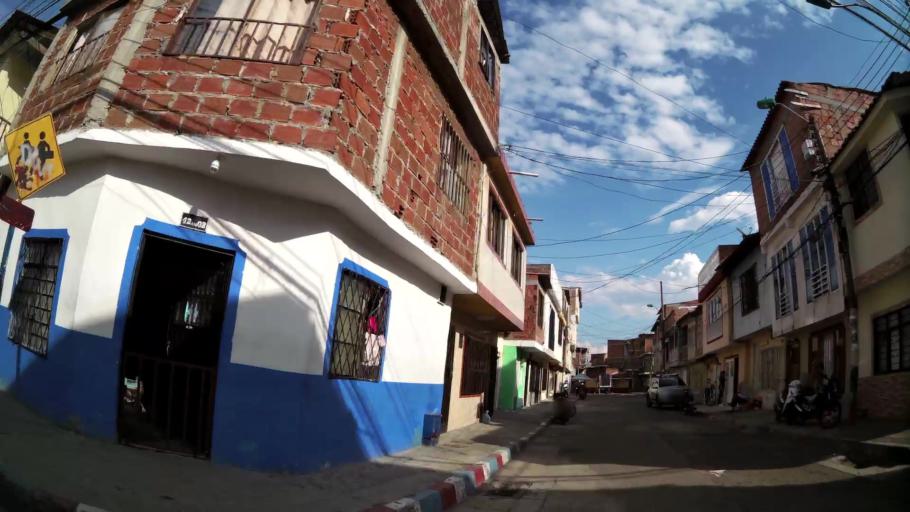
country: CO
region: Valle del Cauca
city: Cali
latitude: 3.4748
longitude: -76.5184
